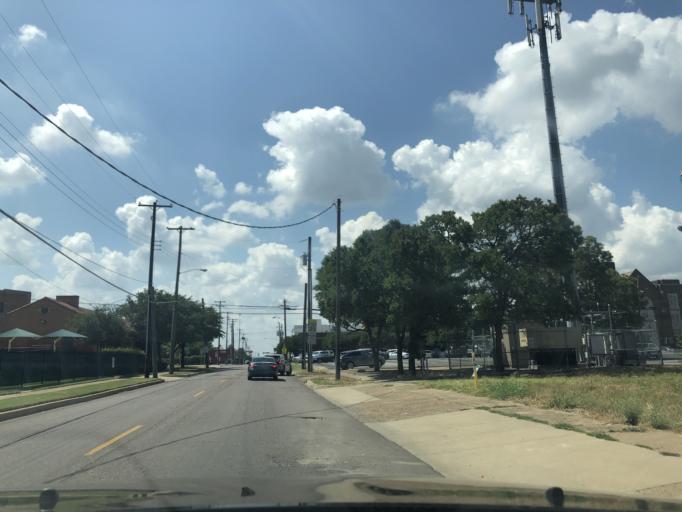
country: US
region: Texas
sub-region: Dallas County
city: Dallas
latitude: 32.7463
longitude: -96.8229
